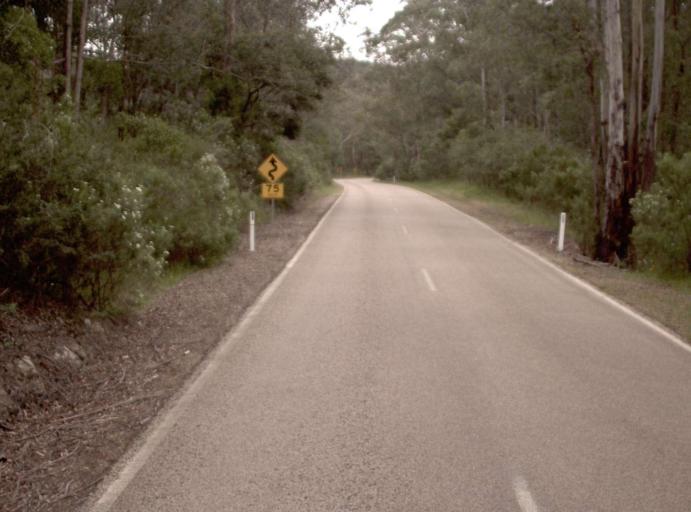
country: AU
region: Victoria
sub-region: East Gippsland
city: Bairnsdale
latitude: -37.6296
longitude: 147.2184
